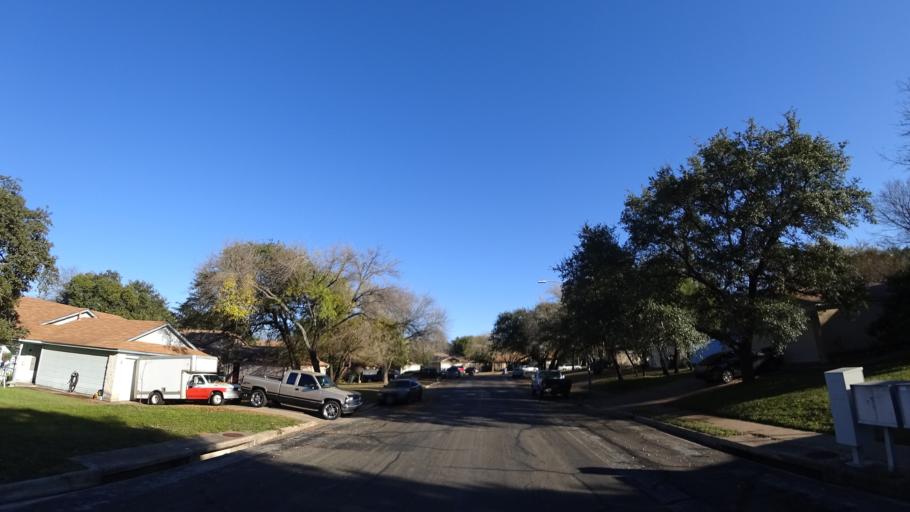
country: US
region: Texas
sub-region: Travis County
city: Wells Branch
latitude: 30.4003
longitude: -97.7023
